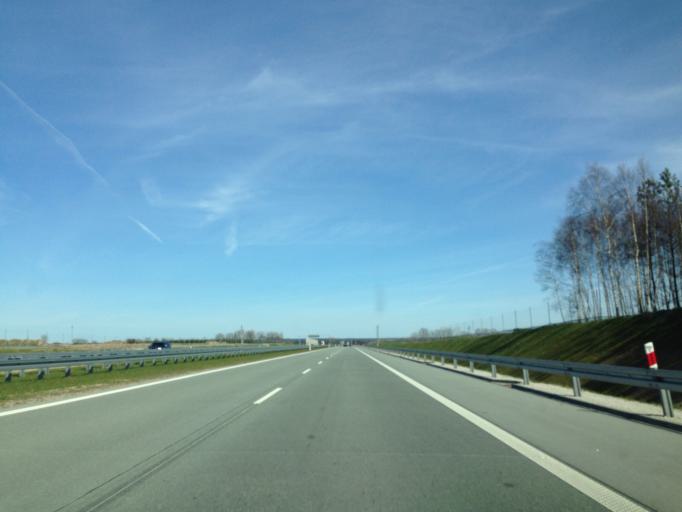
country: PL
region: Lodz Voivodeship
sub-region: Powiat sieradzki
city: Sieradz
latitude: 51.5611
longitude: 18.7431
